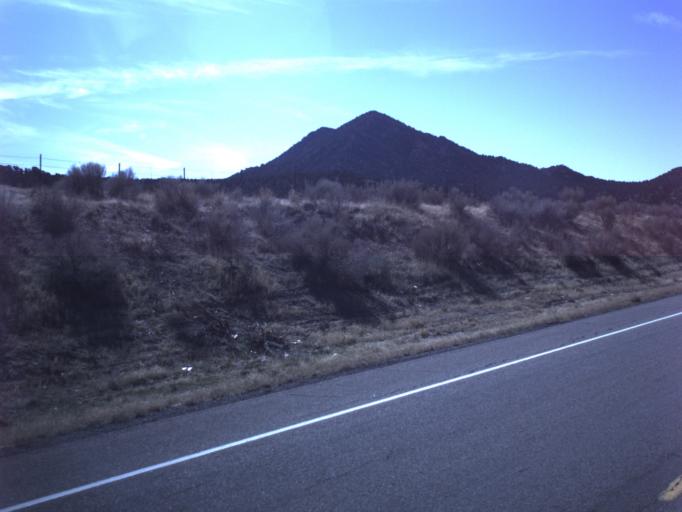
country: US
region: Utah
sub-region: Juab County
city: Nephi
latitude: 39.4328
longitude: -111.9177
